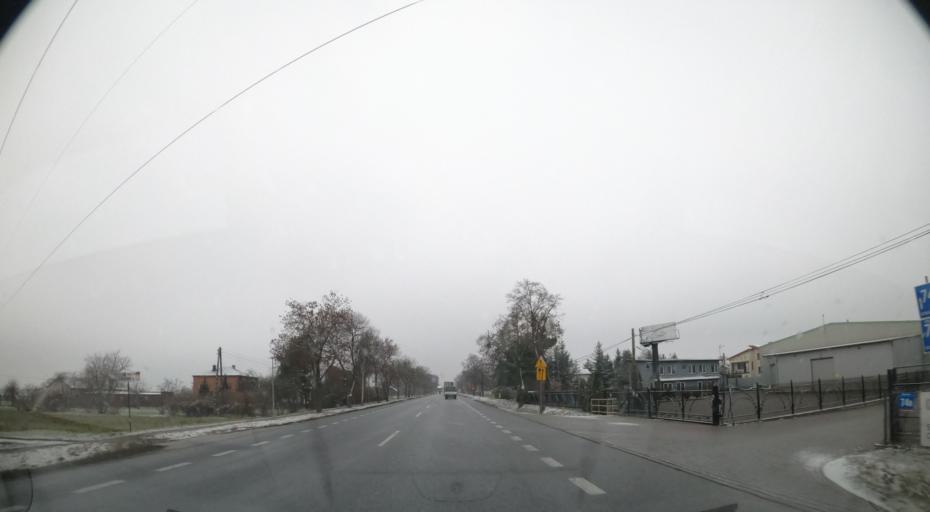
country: PL
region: Masovian Voivodeship
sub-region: Powiat warszawski zachodni
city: Blonie
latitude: 52.1996
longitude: 20.5929
